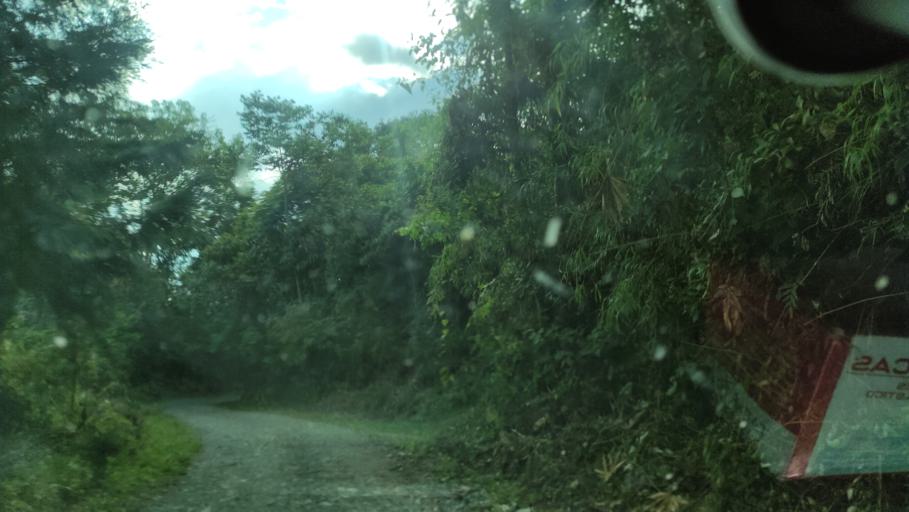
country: CO
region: Valle del Cauca
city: San Pedro
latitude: 3.8807
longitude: -76.1578
